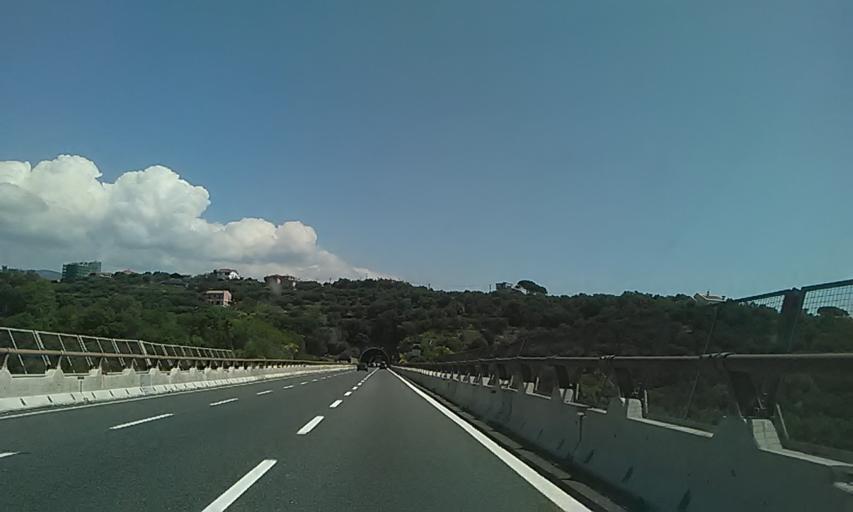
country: IT
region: Liguria
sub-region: Provincia di Savona
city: Celle Ligure
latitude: 44.3380
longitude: 8.5344
